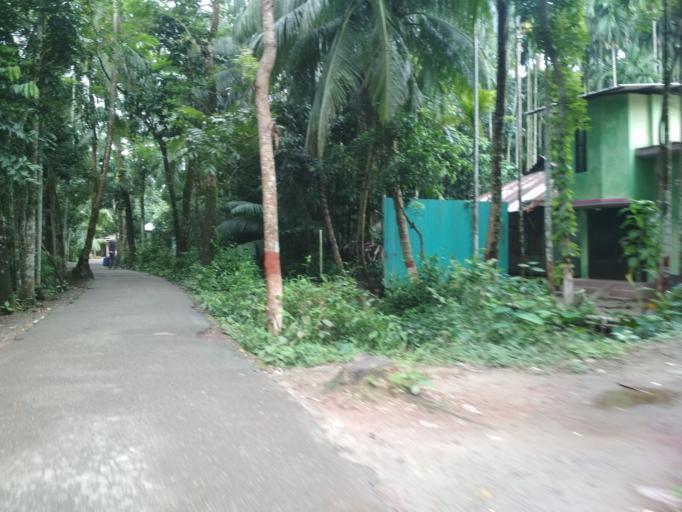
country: BD
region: Chittagong
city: Lakshmipur
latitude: 22.9667
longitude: 90.8036
